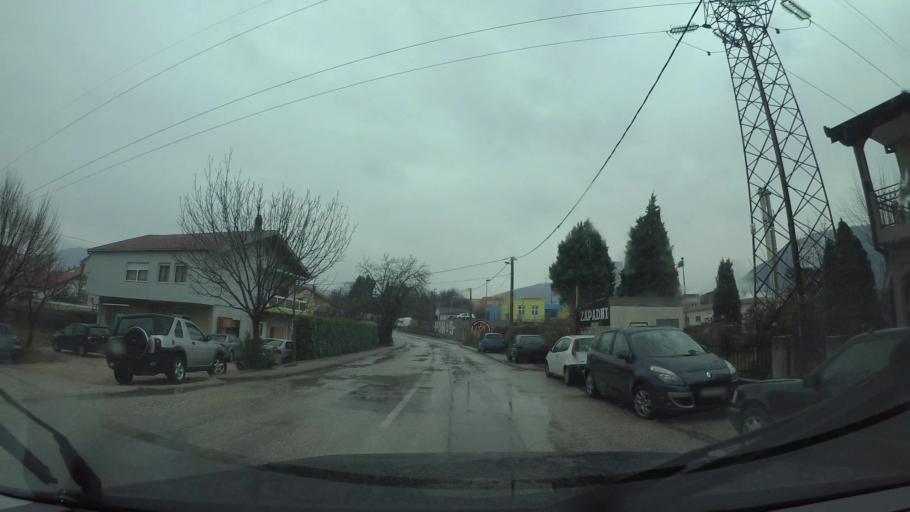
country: BA
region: Federation of Bosnia and Herzegovina
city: Cim
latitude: 43.3472
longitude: 17.7878
